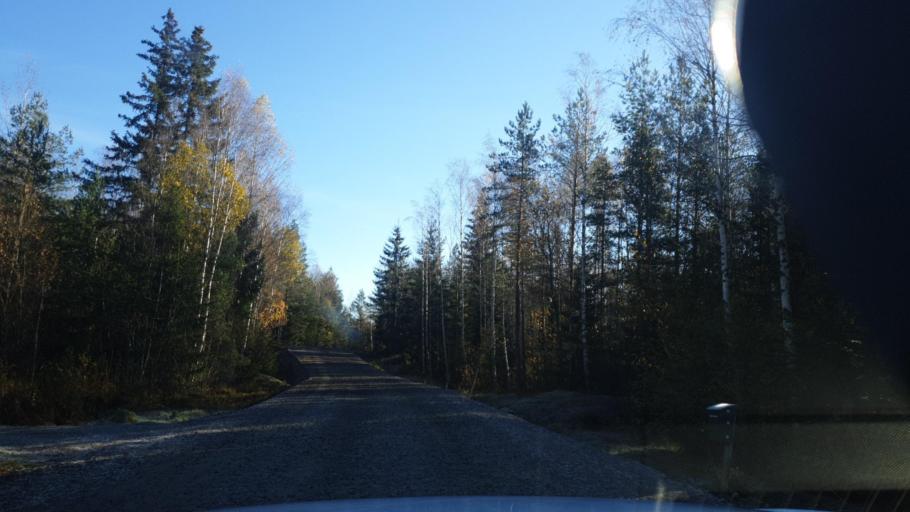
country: SE
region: Vaermland
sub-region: Karlstads Kommun
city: Valberg
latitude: 59.4162
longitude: 13.1260
